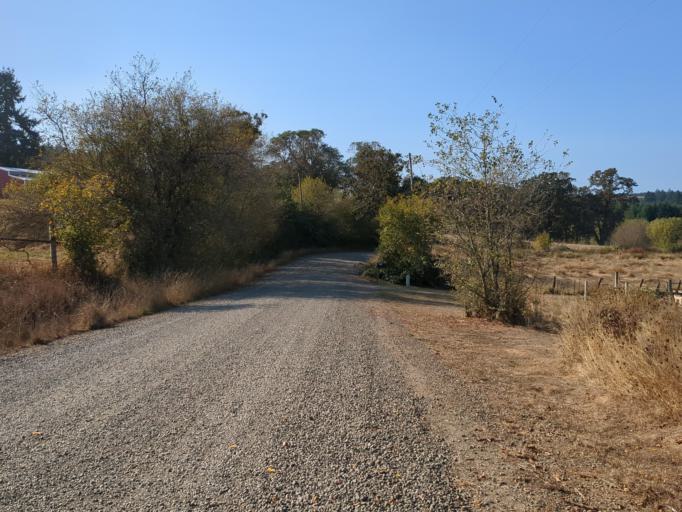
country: US
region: Oregon
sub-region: Lane County
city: Junction City
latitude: 44.2954
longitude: -123.3630
